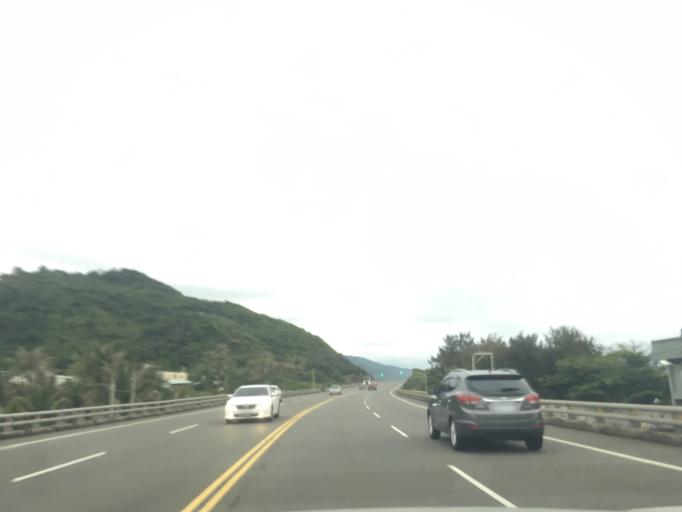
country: TW
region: Taiwan
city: Hengchun
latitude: 22.3074
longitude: 120.8900
